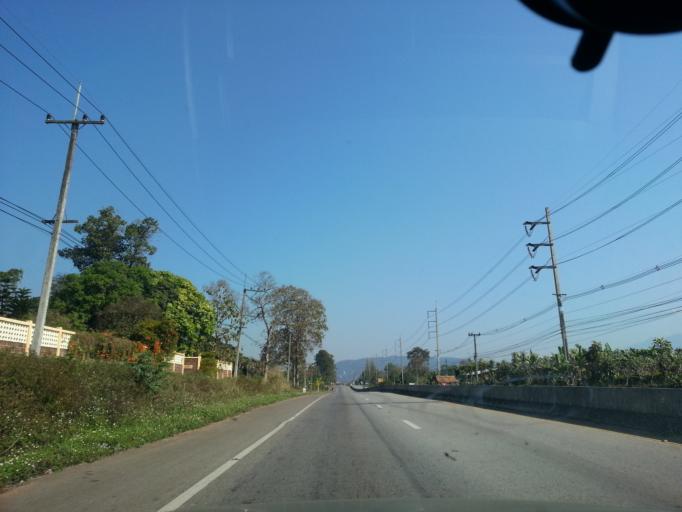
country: TH
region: Chiang Mai
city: Mae Taeng
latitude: 19.1883
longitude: 98.9567
